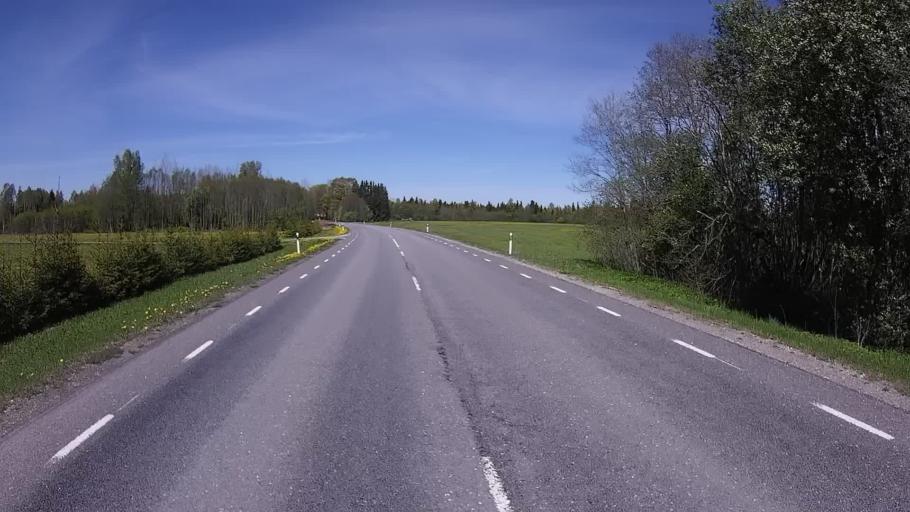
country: EE
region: Raplamaa
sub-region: Kehtna vald
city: Kehtna
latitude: 59.0497
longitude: 25.0233
